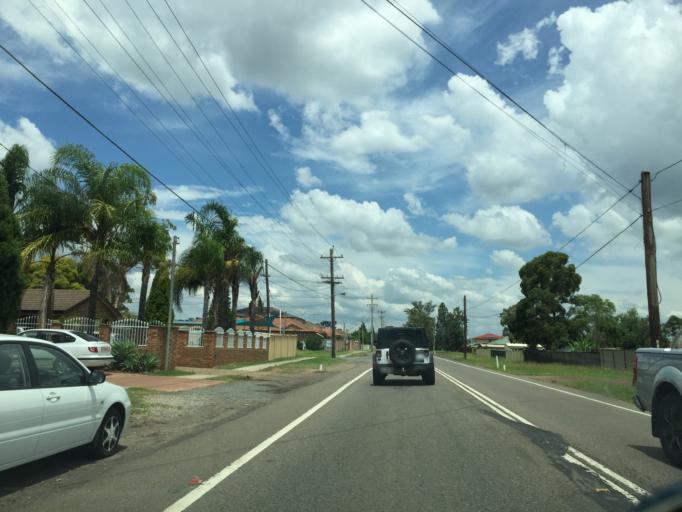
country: AU
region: New South Wales
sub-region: Blacktown
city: Hassall Grove
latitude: -33.7403
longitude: 150.8435
